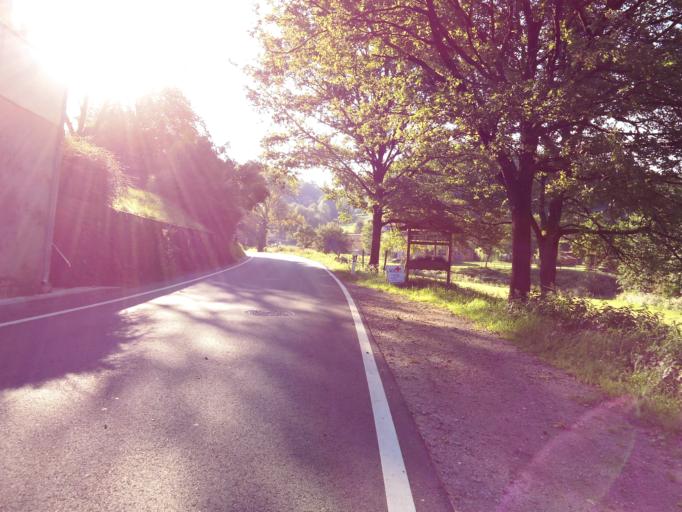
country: DE
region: Hesse
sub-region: Regierungsbezirk Darmstadt
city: Heppenheim an der Bergstrasse
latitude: 49.6667
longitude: 8.6800
